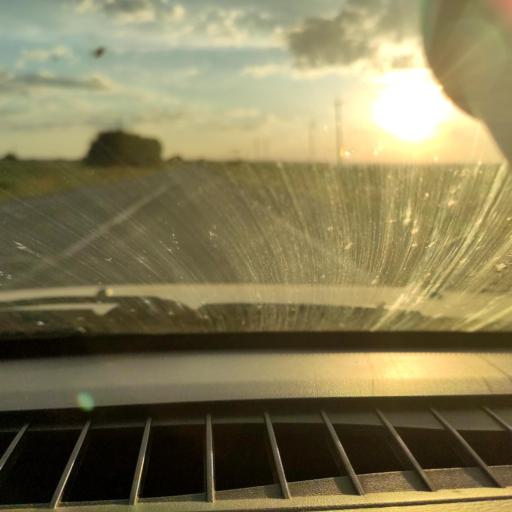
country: RU
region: Kirov
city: Kotel'nich
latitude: 58.3220
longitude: 48.3755
